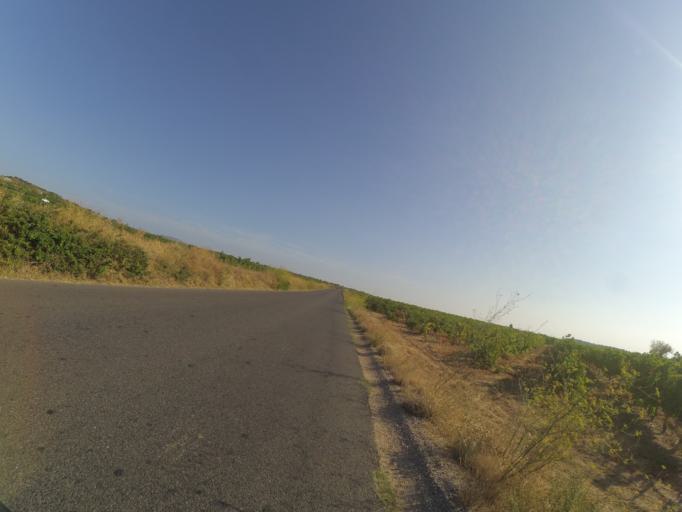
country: FR
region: Languedoc-Roussillon
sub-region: Departement des Pyrenees-Orientales
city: Baixas
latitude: 42.7582
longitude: 2.8190
